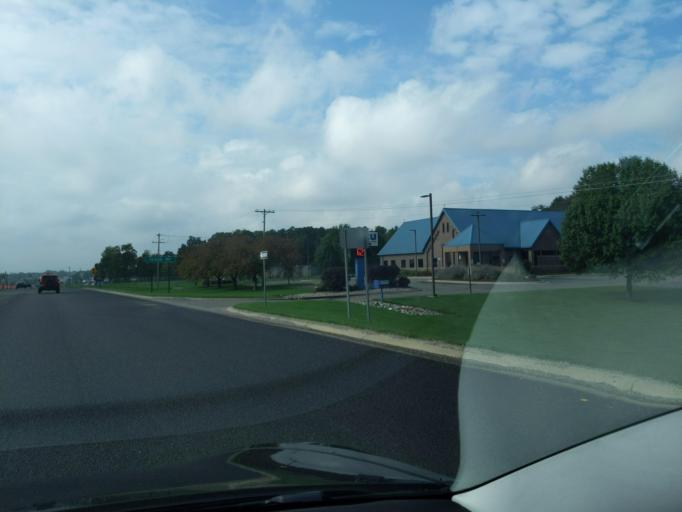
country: US
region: Michigan
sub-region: Eaton County
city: Charlotte
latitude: 42.5837
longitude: -84.8058
